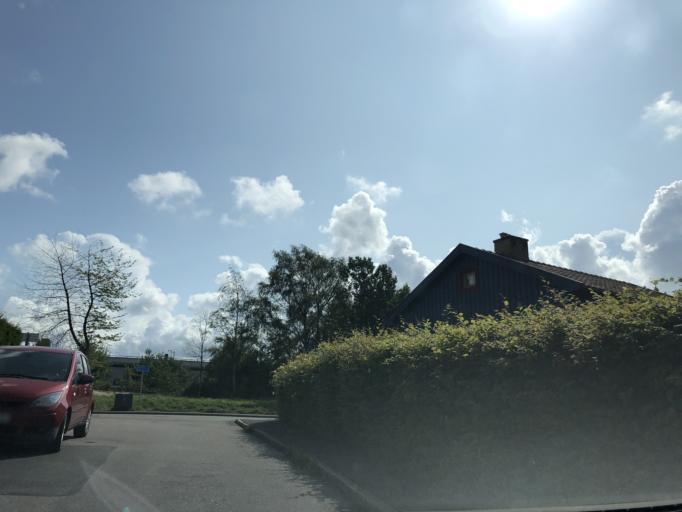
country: SE
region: Vaestra Goetaland
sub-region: Goteborg
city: Majorna
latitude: 57.7199
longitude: 11.8993
